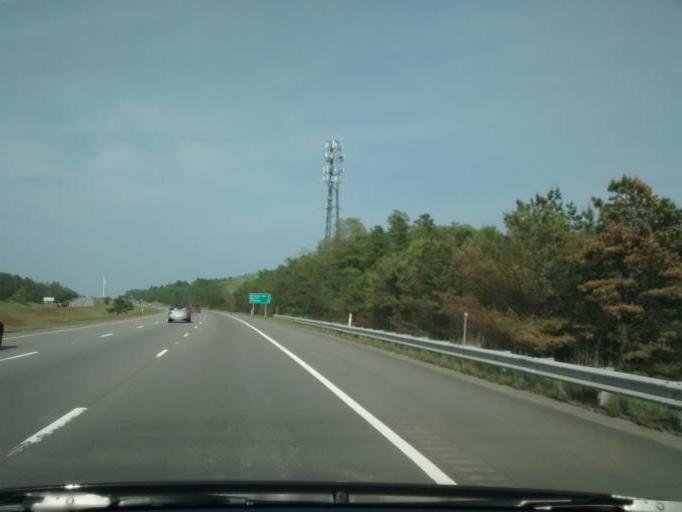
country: US
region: Massachusetts
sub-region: Plymouth County
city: Onset
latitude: 41.7652
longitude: -70.6555
